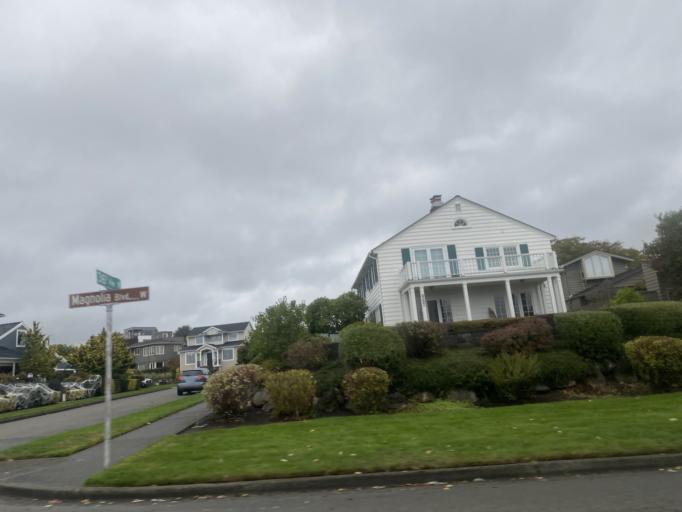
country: US
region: Washington
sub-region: King County
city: Seattle
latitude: 47.6348
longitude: -122.4038
